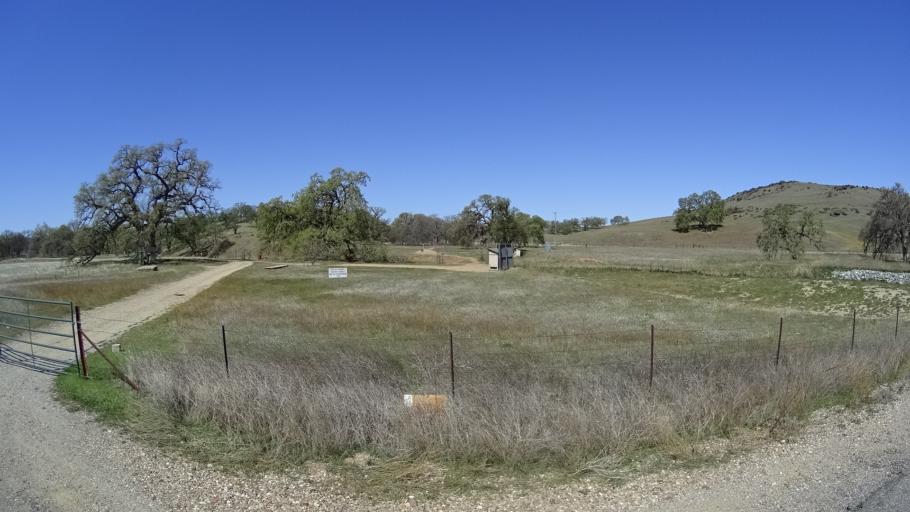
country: US
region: California
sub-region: Glenn County
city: Orland
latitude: 39.7617
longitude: -122.3415
